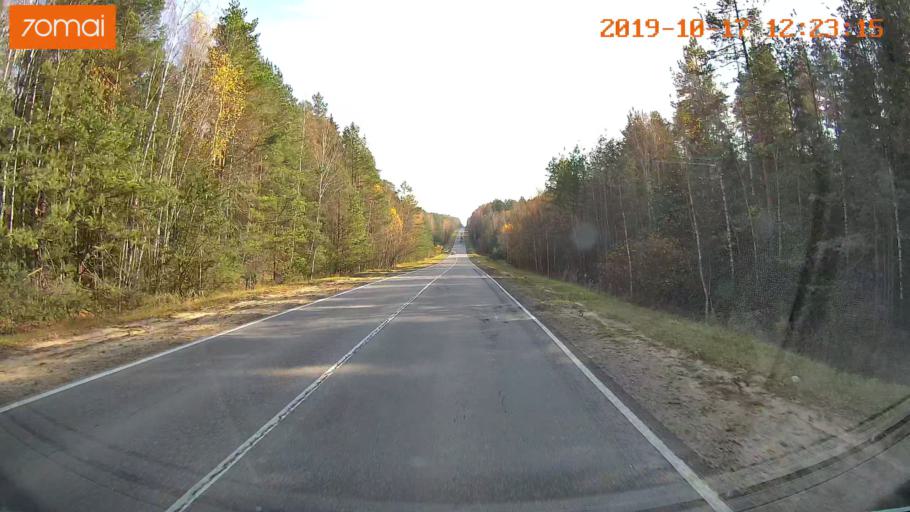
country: RU
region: Rjazan
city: Gus'-Zheleznyy
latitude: 55.0456
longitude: 41.1893
